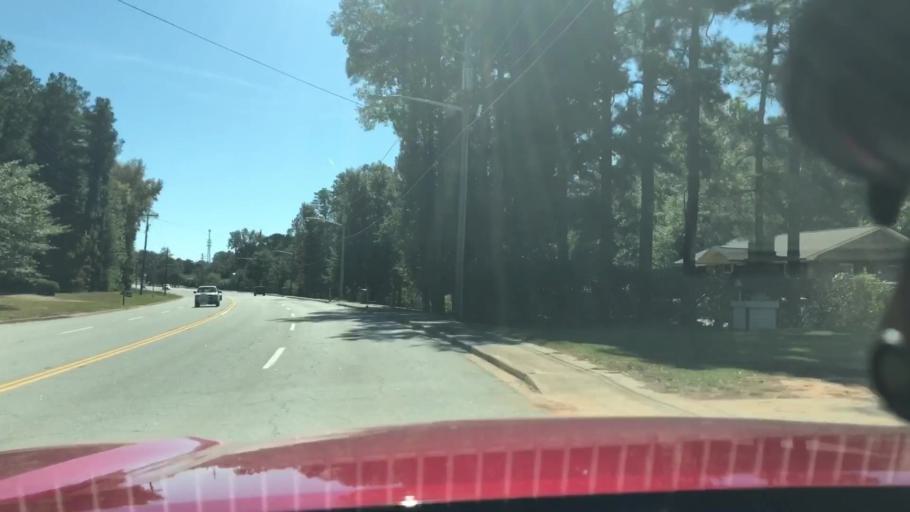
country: US
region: South Carolina
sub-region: Greenwood County
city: Greenwood
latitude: 34.2245
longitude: -82.1418
